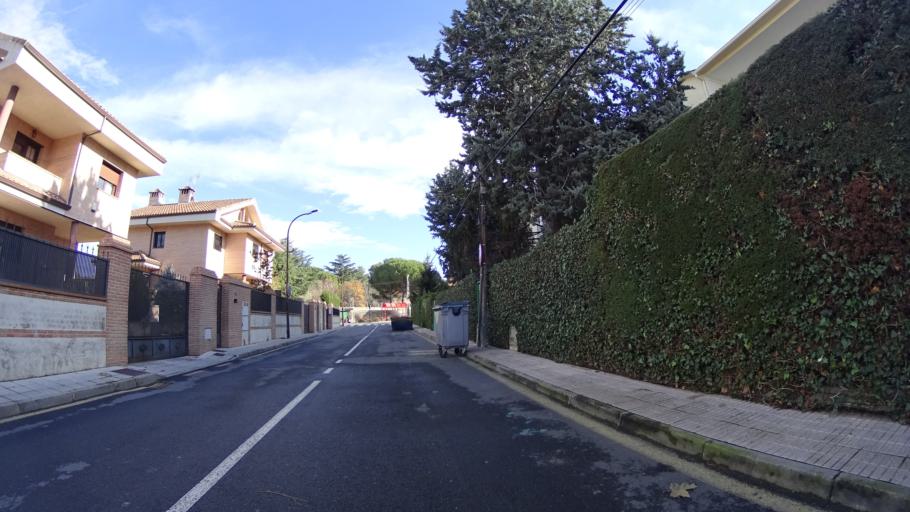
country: ES
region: Madrid
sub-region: Provincia de Madrid
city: Galapagar
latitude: 40.5758
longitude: -4.0107
